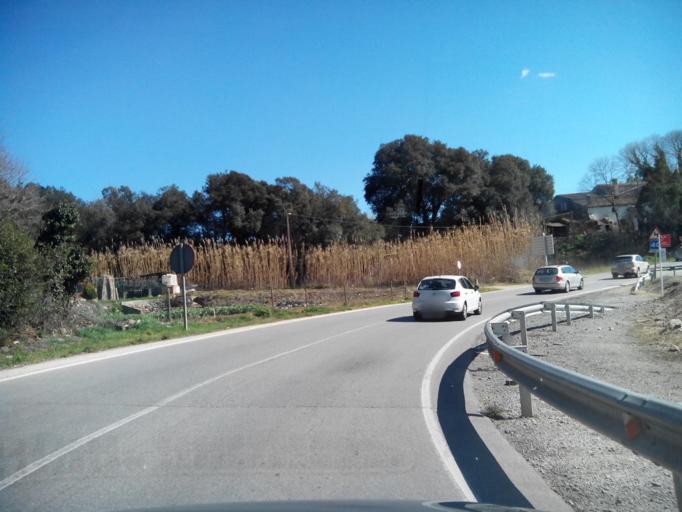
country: ES
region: Catalonia
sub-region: Provincia de Barcelona
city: Dosrius
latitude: 41.5988
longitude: 2.4100
